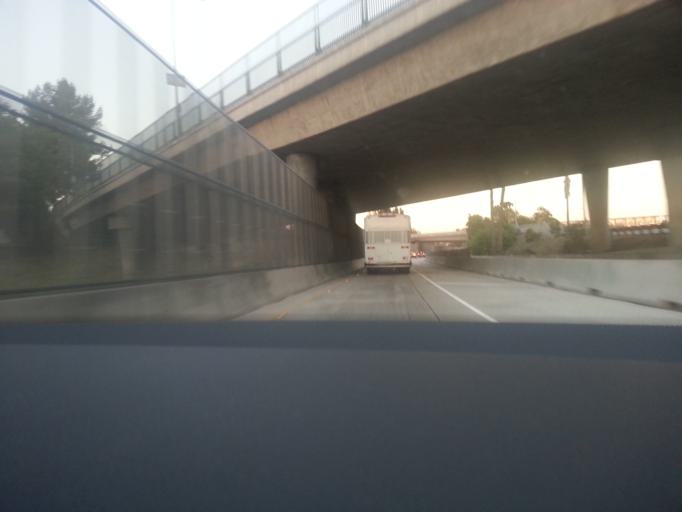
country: US
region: California
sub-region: Los Angeles County
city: Boyle Heights
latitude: 34.0552
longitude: -118.2030
